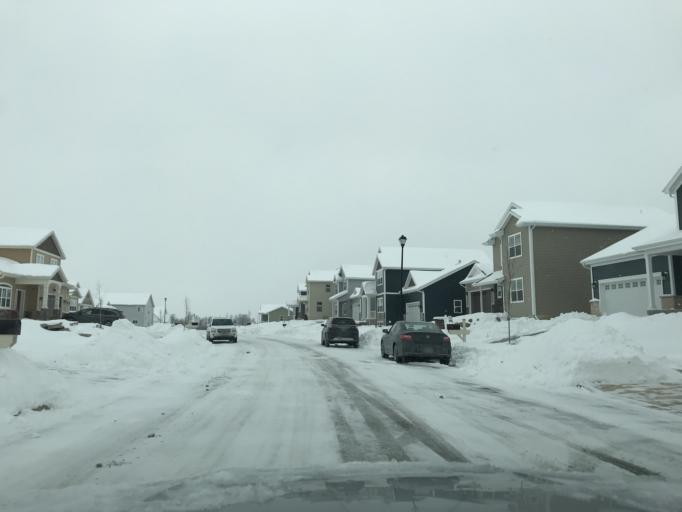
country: US
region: Wisconsin
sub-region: Dane County
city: Sun Prairie
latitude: 43.1735
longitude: -89.2727
